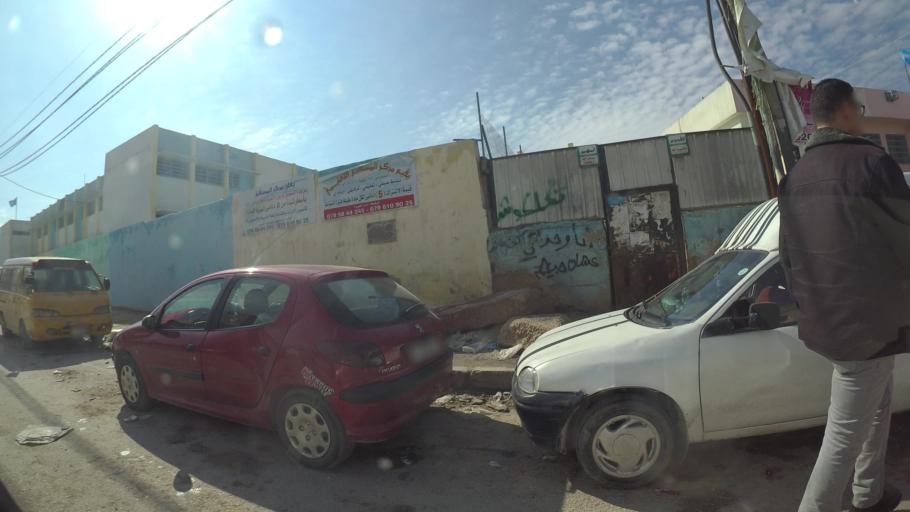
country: JO
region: Amman
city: Al Jubayhah
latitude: 32.0653
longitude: 35.8416
